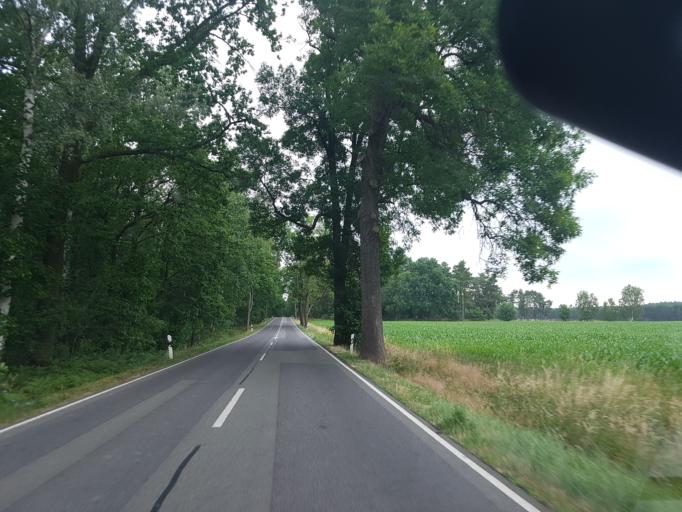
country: DE
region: Brandenburg
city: Lebusa
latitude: 51.8127
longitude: 13.4204
